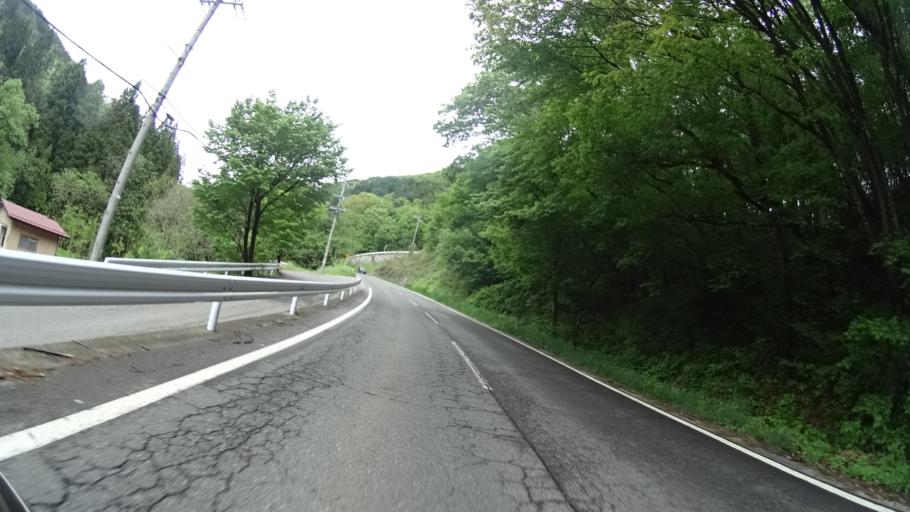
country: JP
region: Nagano
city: Nagano-shi
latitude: 36.6920
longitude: 138.2051
